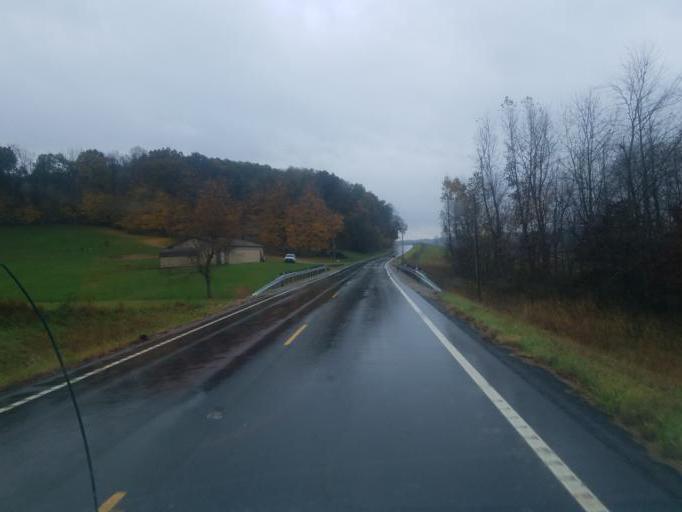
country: US
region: Ohio
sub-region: Muskingum County
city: Frazeysburg
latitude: 40.1443
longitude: -82.2145
